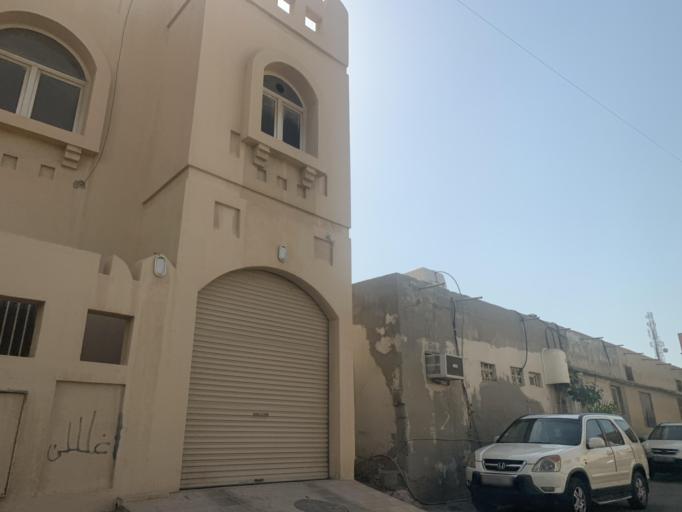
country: BH
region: Northern
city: Madinat `Isa
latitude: 26.1938
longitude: 50.4889
